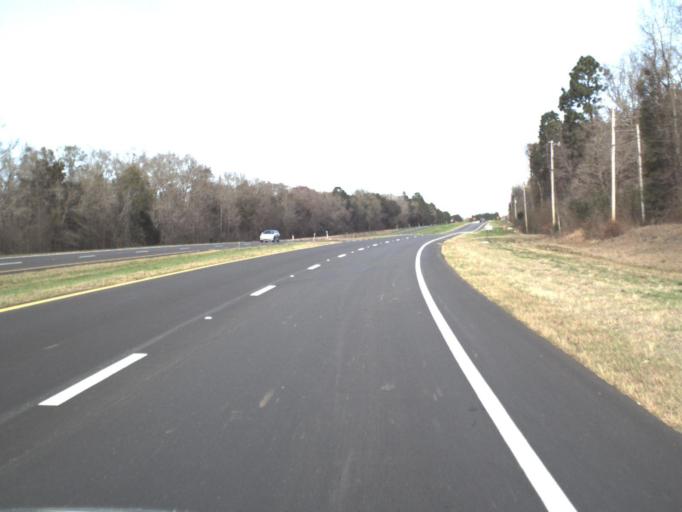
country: US
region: Florida
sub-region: Washington County
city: Chipley
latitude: 30.6743
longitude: -85.3940
